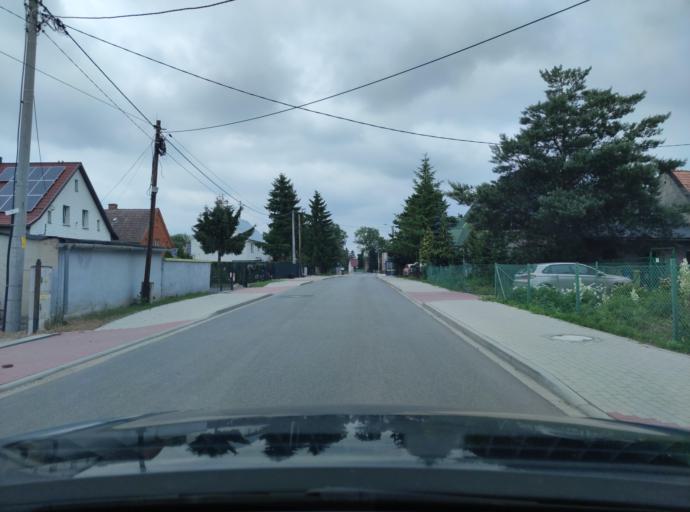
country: PL
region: Lower Silesian Voivodeship
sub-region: Powiat wroclawski
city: Kobierzyce
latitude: 50.9748
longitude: 16.9050
